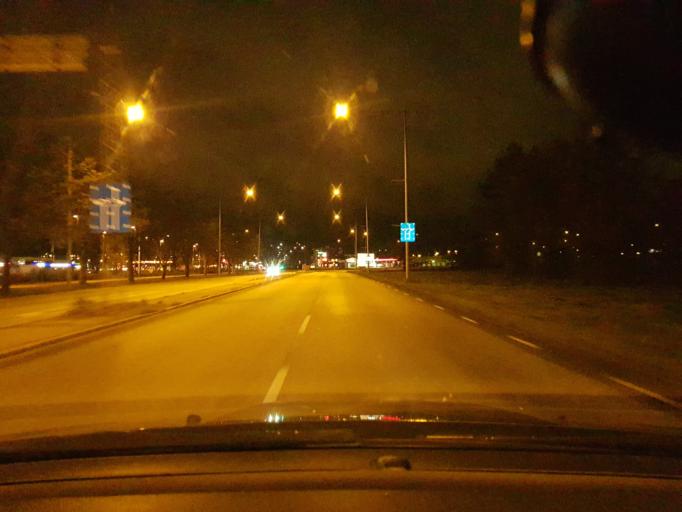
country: SE
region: Uppsala
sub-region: Uppsala Kommun
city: Uppsala
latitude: 59.8455
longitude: 17.6671
